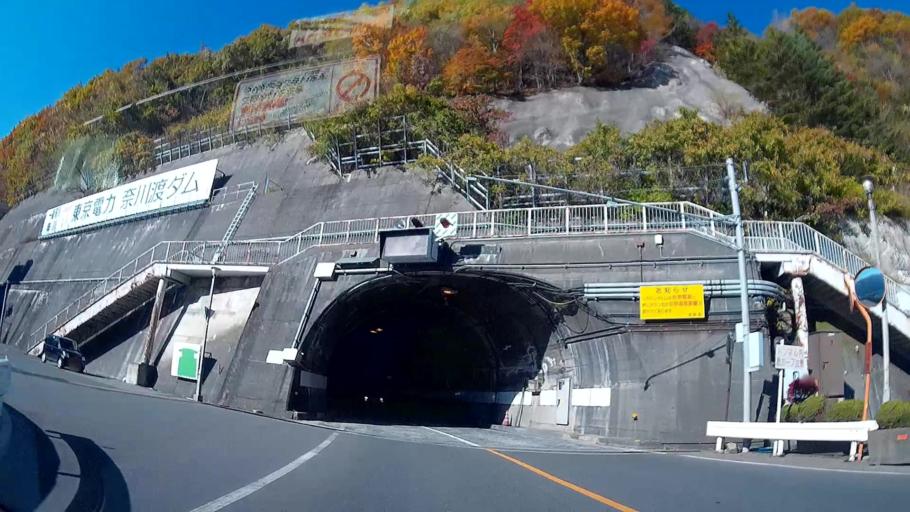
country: JP
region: Nagano
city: Toyoshina
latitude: 36.1339
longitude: 137.7184
